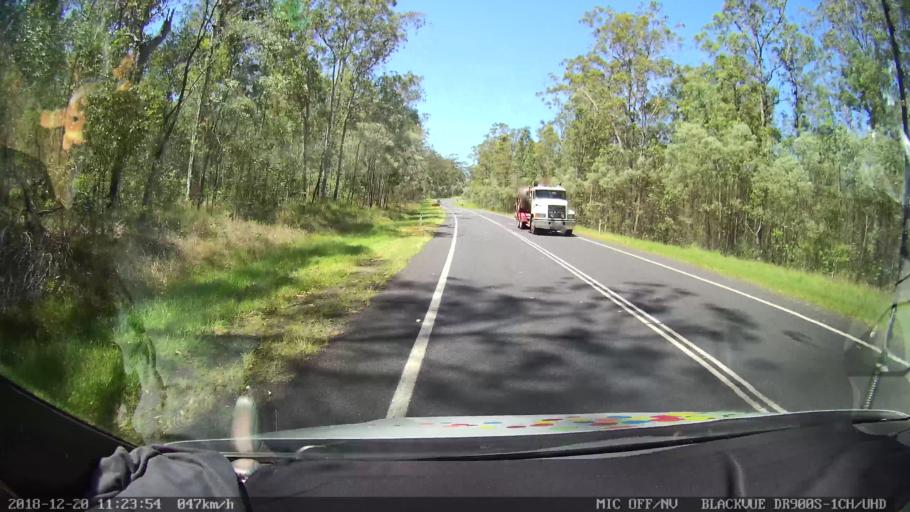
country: AU
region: New South Wales
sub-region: Richmond Valley
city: Casino
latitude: -29.0683
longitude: 153.0036
